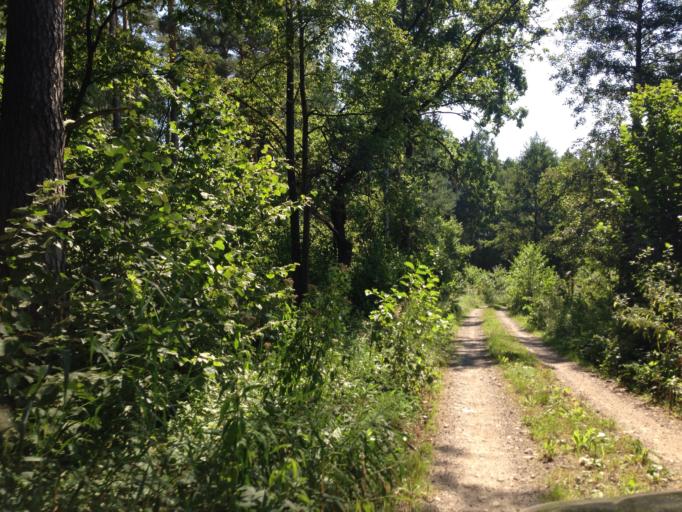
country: PL
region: Kujawsko-Pomorskie
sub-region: Powiat brodnicki
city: Bartniczka
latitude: 53.2789
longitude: 19.5732
